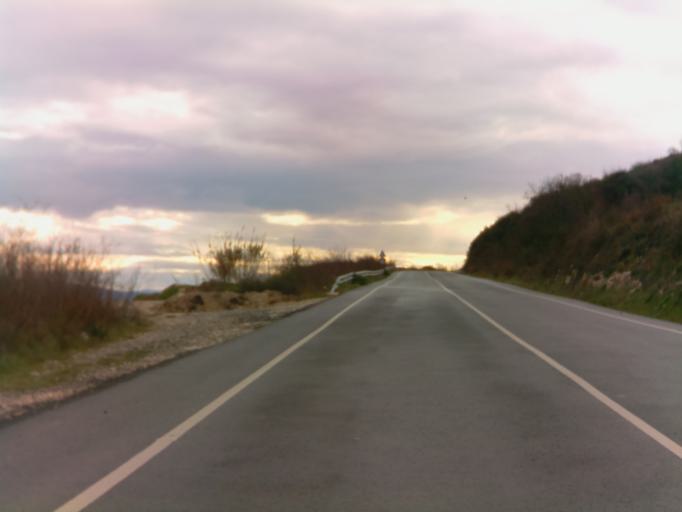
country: CY
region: Pafos
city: Pegeia
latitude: 34.9068
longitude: 32.4401
